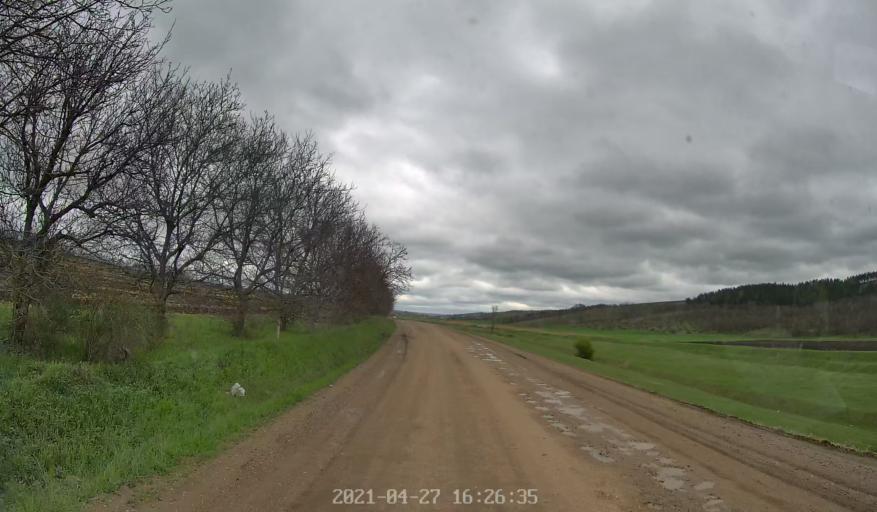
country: MD
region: Chisinau
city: Singera
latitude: 46.9790
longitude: 29.0272
